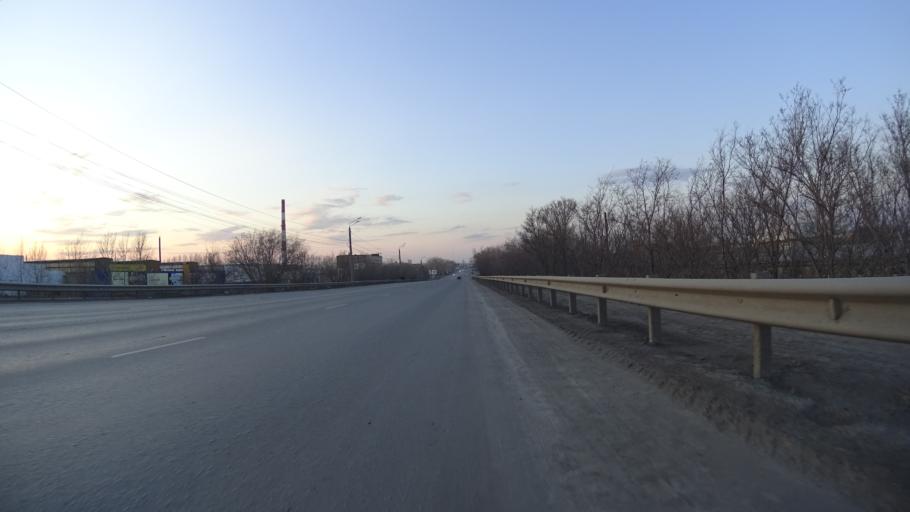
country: RU
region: Chelyabinsk
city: Novosineglazovskiy
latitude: 55.1029
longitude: 61.3877
